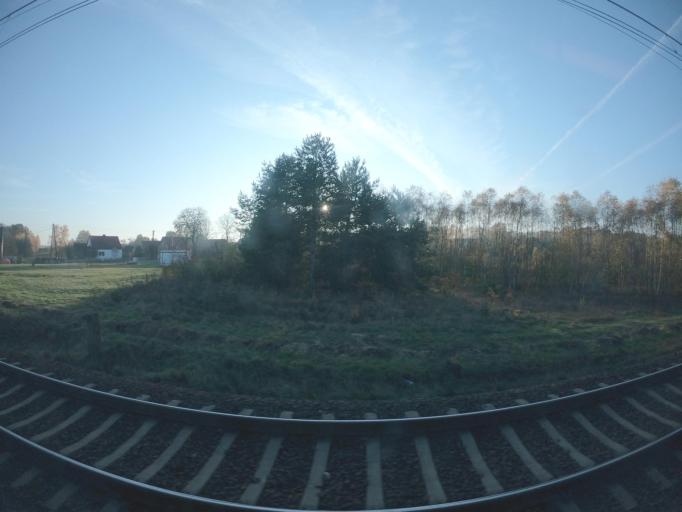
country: PL
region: Lubusz
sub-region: Powiat sulecinski
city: Torzym
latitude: 52.2558
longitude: 14.9506
